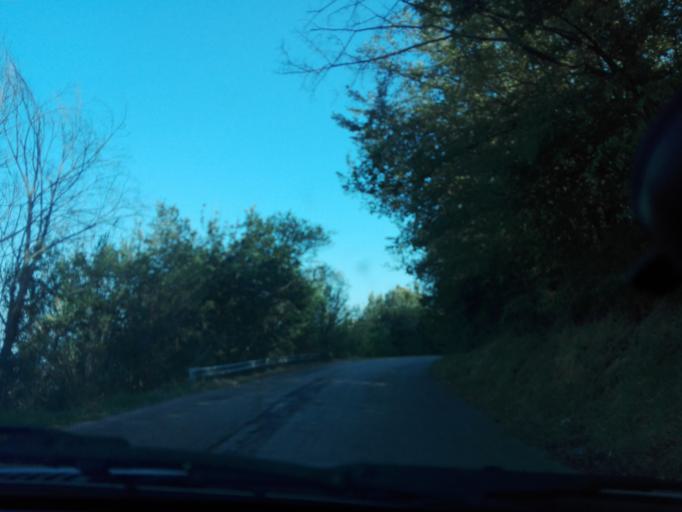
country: IT
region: Abruzzo
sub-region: Provincia di Pescara
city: Cappelle sul Tavo
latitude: 42.4439
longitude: 14.0944
